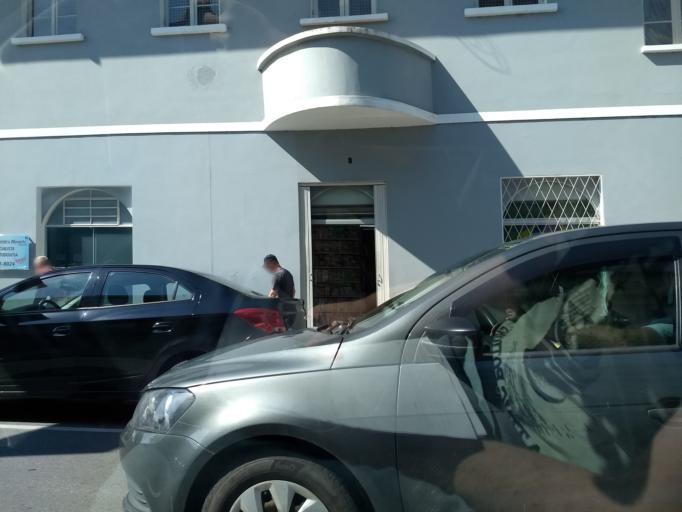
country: BR
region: Santa Catarina
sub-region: Jaragua Do Sul
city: Jaragua do Sul
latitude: -26.4809
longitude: -49.0834
